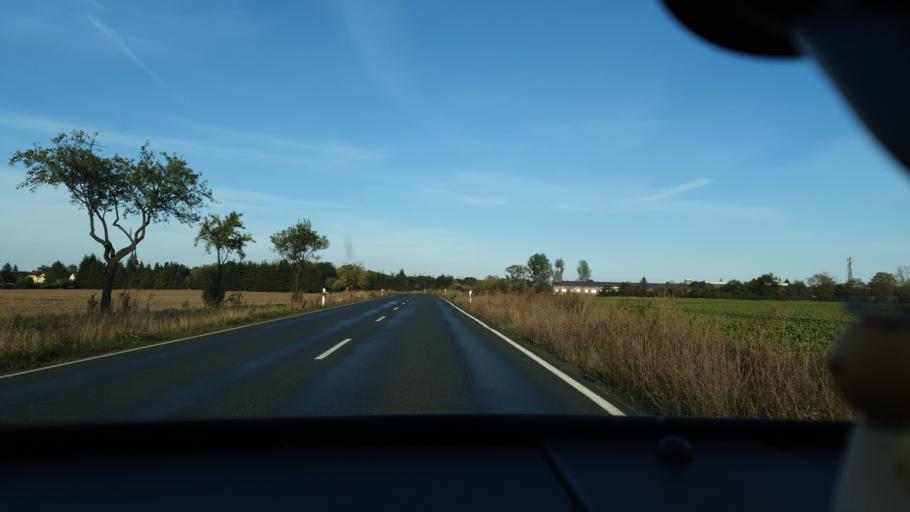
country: DE
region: Saxony
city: Krostitz
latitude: 51.4565
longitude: 12.4453
